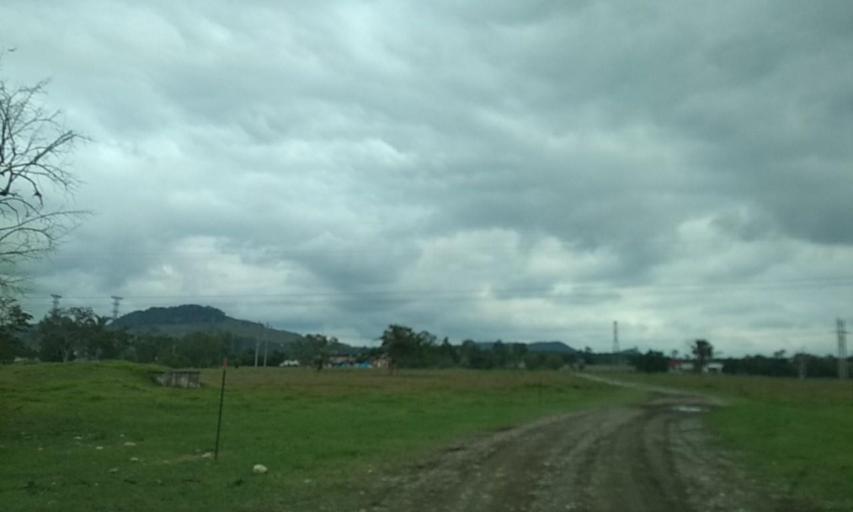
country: MX
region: Veracruz
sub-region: Papantla
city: El Chote
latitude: 20.3922
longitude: -97.3416
